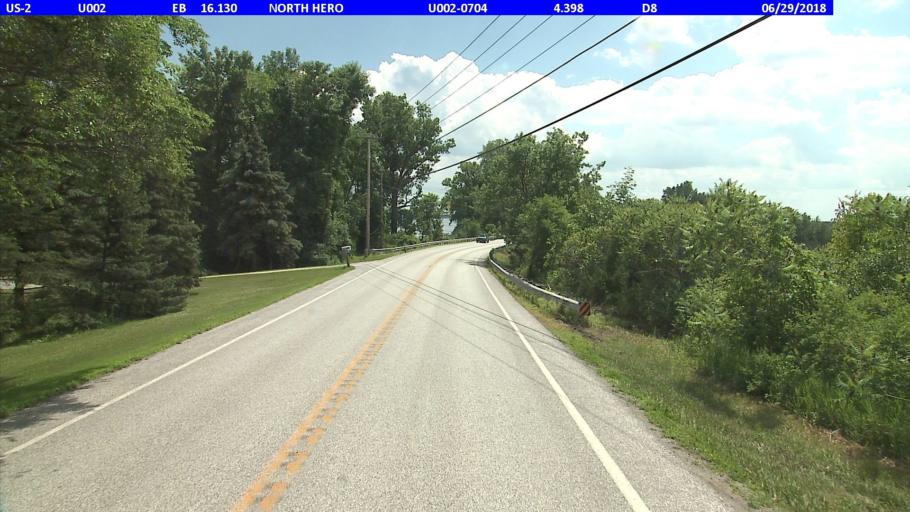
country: US
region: Vermont
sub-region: Grand Isle County
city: North Hero
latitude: 44.8308
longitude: -73.2741
